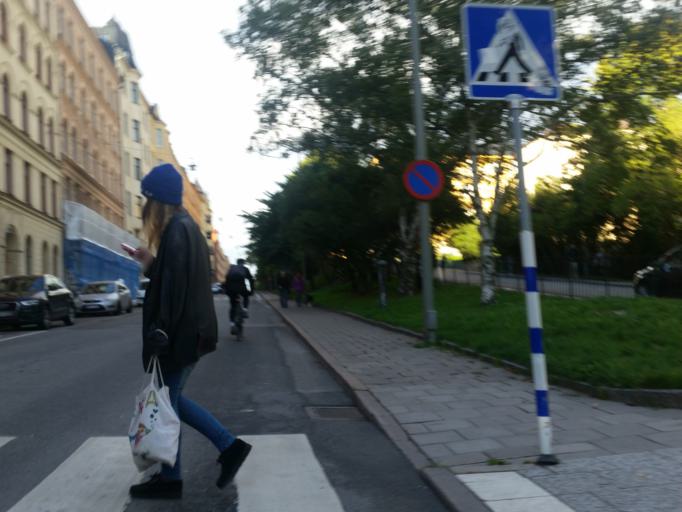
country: SE
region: Stockholm
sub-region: Stockholms Kommun
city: Stockholm
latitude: 59.3188
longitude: 18.0492
